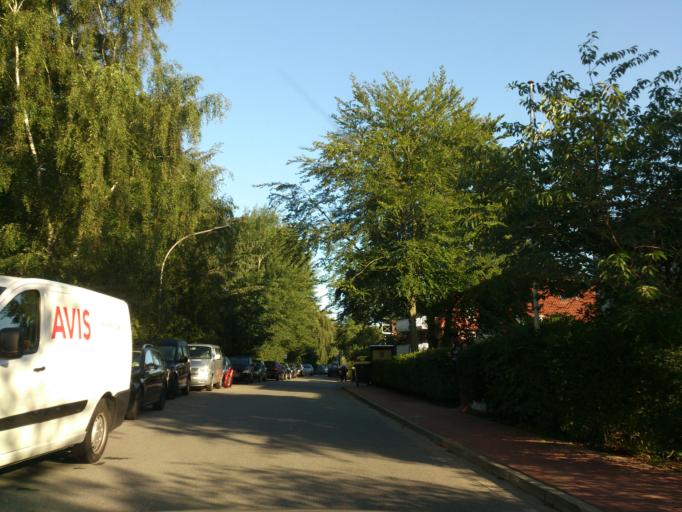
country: DE
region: Schleswig-Holstein
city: Sankt Peter-Ording
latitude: 54.3210
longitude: 8.6140
